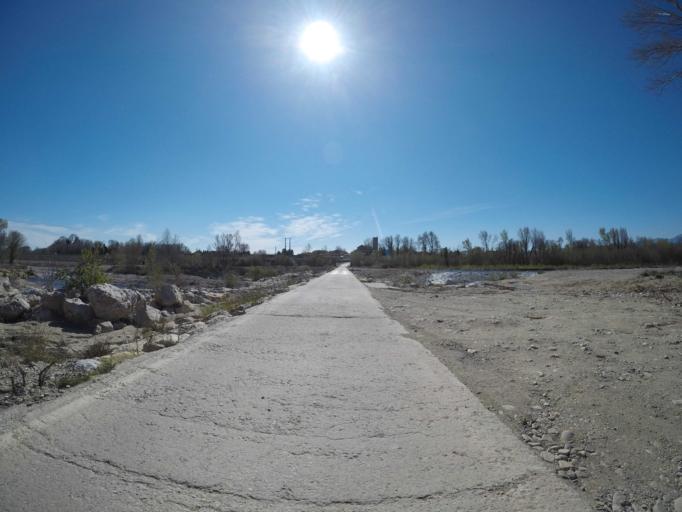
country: FR
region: Languedoc-Roussillon
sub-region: Departement des Pyrenees-Orientales
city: Millas
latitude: 42.6972
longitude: 2.6643
